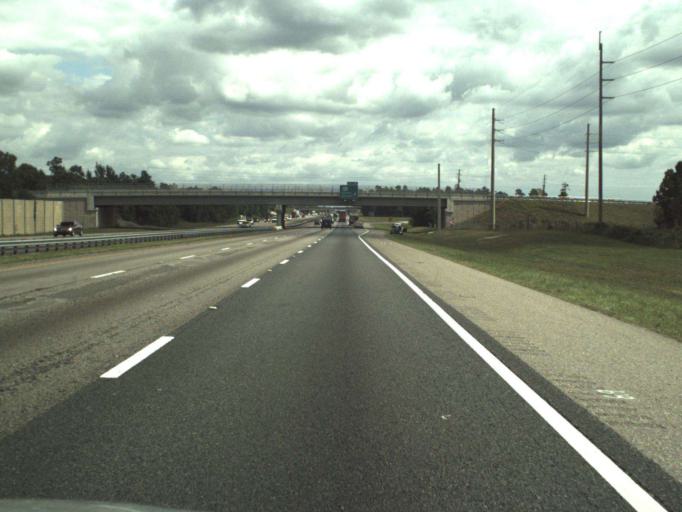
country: US
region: Florida
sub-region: Volusia County
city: Orange City
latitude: 28.9465
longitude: -81.2603
